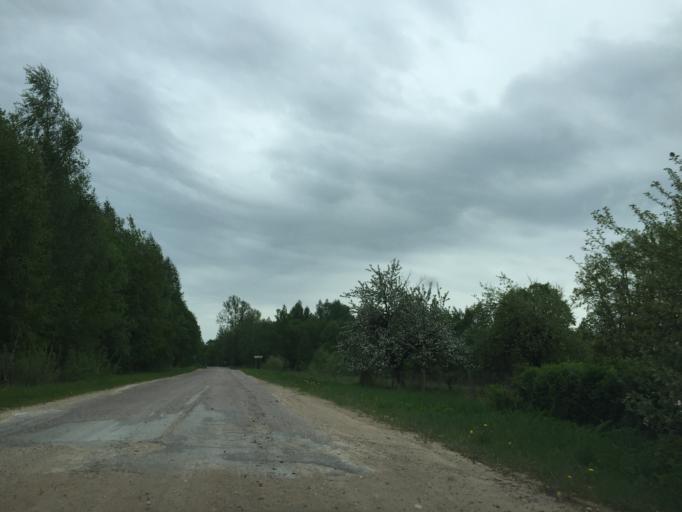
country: LV
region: Lielvarde
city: Lielvarde
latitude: 56.8033
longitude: 24.8630
